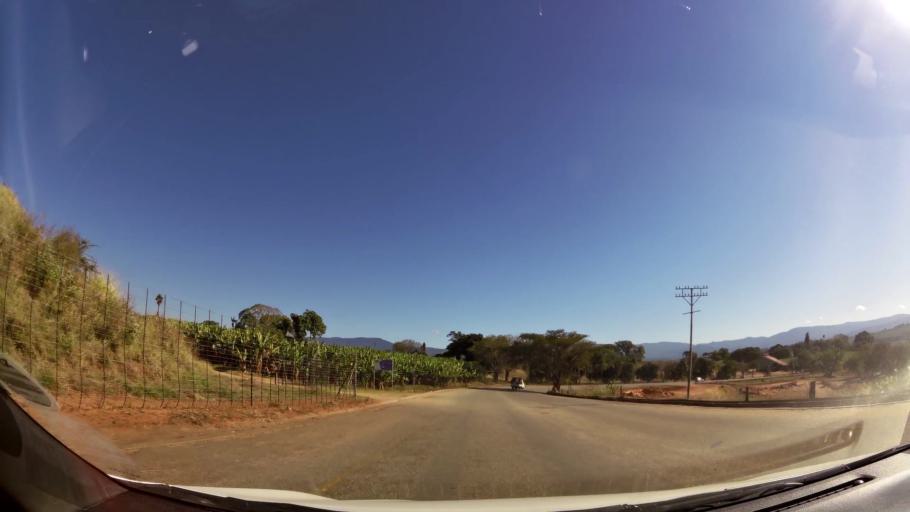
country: ZA
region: Limpopo
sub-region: Mopani District Municipality
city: Tzaneen
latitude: -23.8366
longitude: 30.1341
